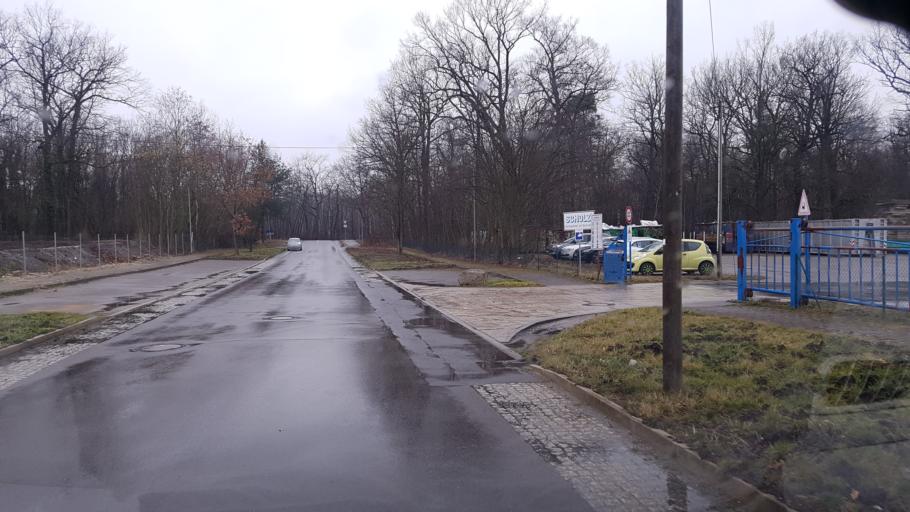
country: DE
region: Brandenburg
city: Lauchhammer
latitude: 51.5080
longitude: 13.8023
